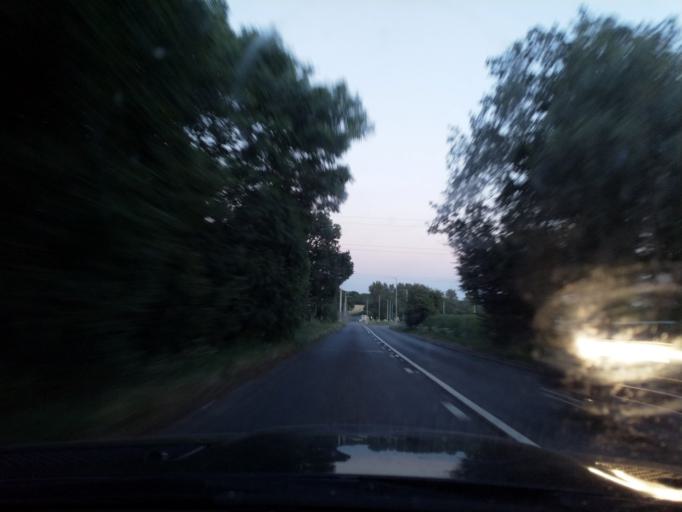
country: GB
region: England
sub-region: Solihull
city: Balsall Common
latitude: 52.3756
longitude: -1.6351
